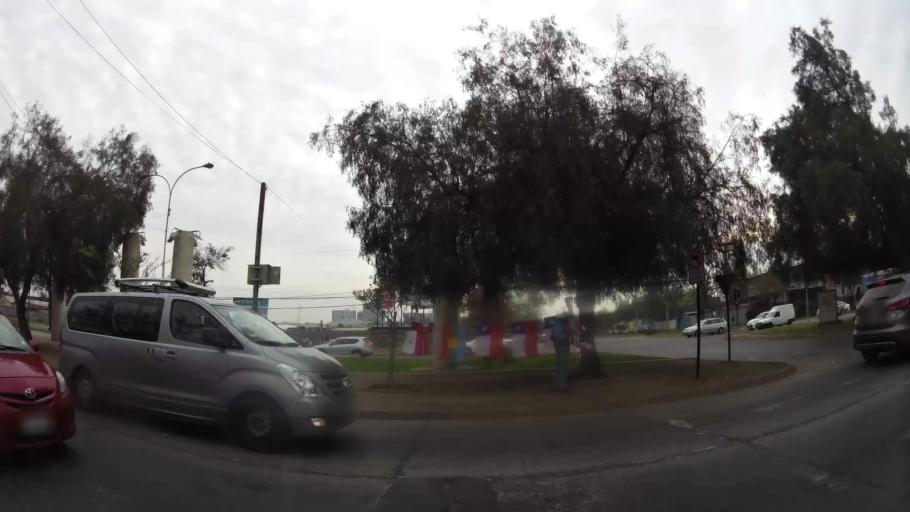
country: CL
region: Santiago Metropolitan
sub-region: Provincia de Santiago
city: Villa Presidente Frei, Nunoa, Santiago, Chile
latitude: -33.4747
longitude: -70.6134
